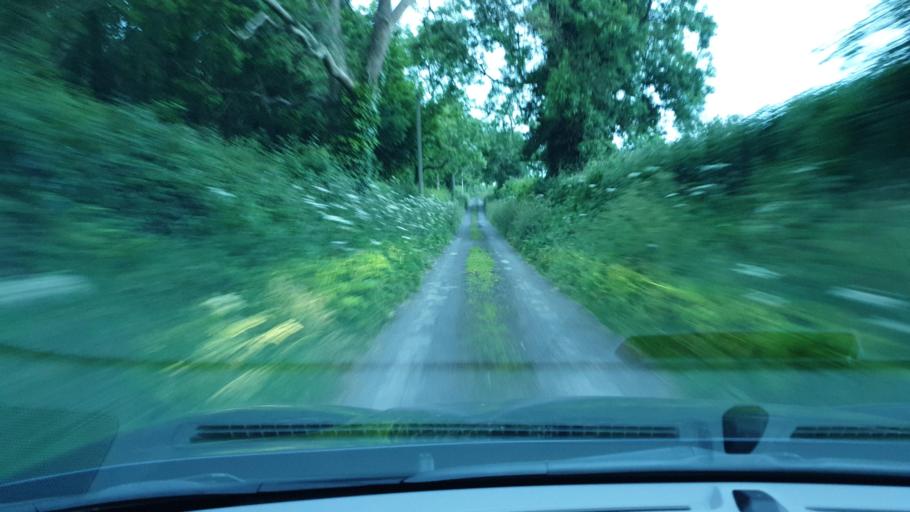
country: IE
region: Leinster
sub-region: An Mhi
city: Duleek
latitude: 53.5947
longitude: -6.3644
